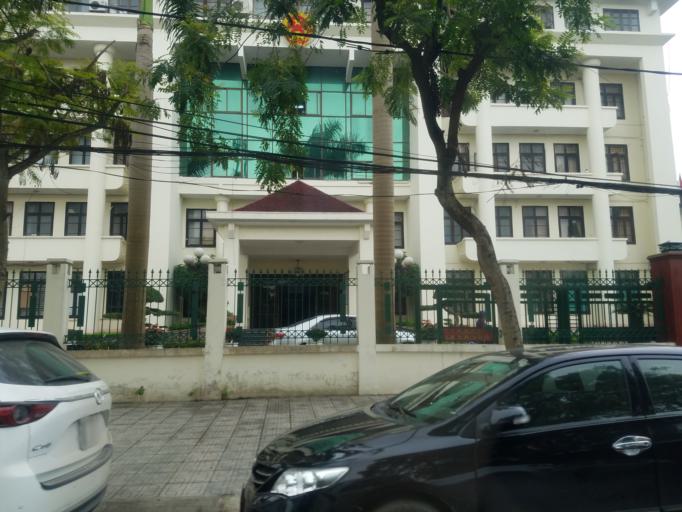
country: VN
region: Thai Nguyen
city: Thanh Pho Thai Nguyen
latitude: 21.5946
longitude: 105.8420
